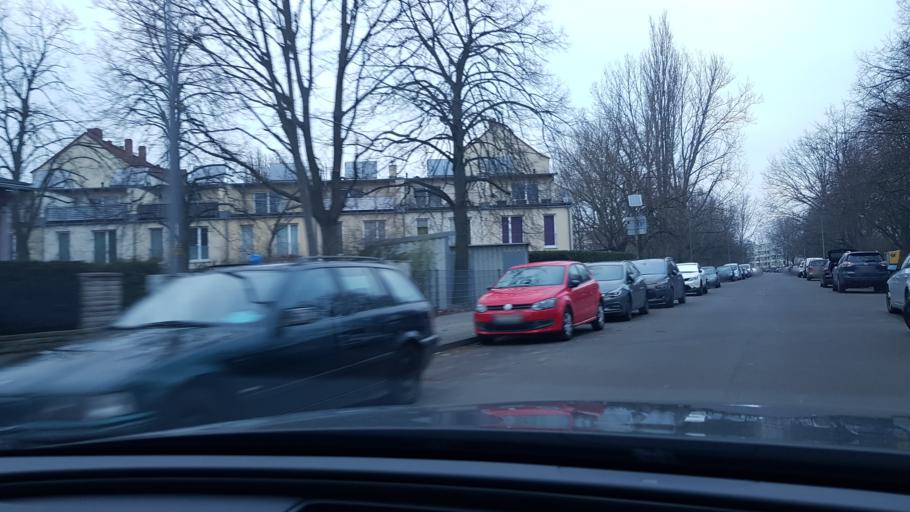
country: DE
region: Berlin
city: Grunau
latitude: 52.4236
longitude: 13.5914
